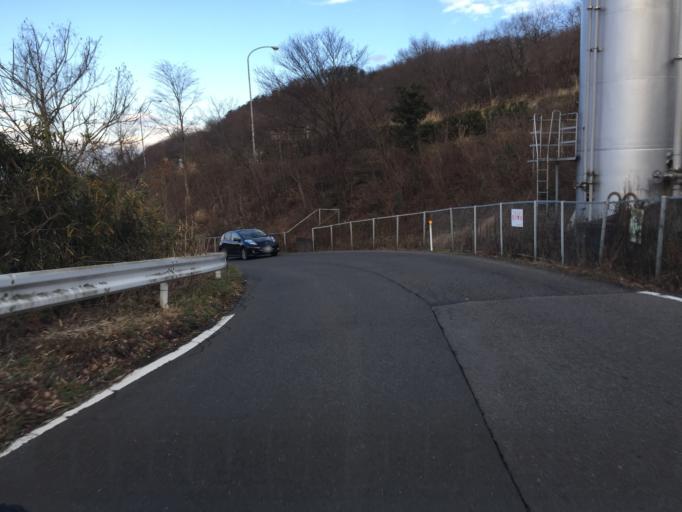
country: JP
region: Fukushima
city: Fukushima-shi
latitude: 37.6876
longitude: 140.4432
